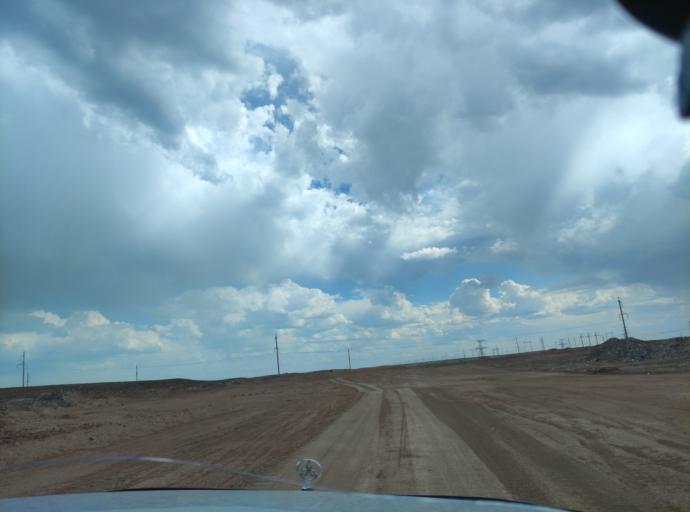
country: KZ
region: Qaraghandy
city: Saryshaghan
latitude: 46.1251
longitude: 73.5963
